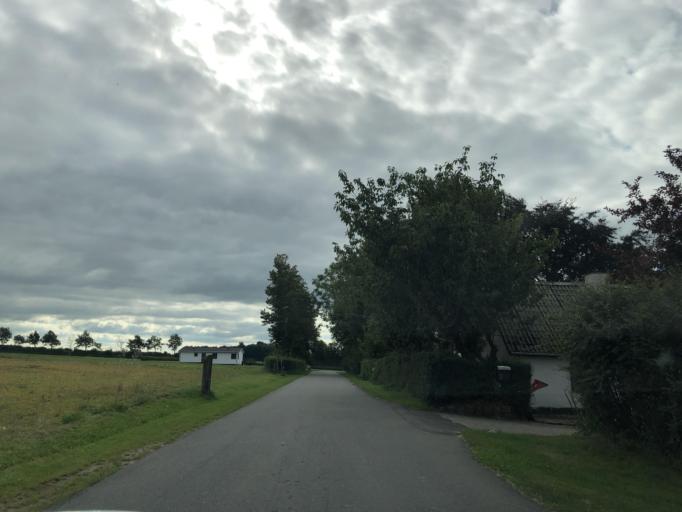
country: DK
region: North Denmark
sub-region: Alborg Kommune
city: Nibe
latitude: 56.8408
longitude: 9.6744
